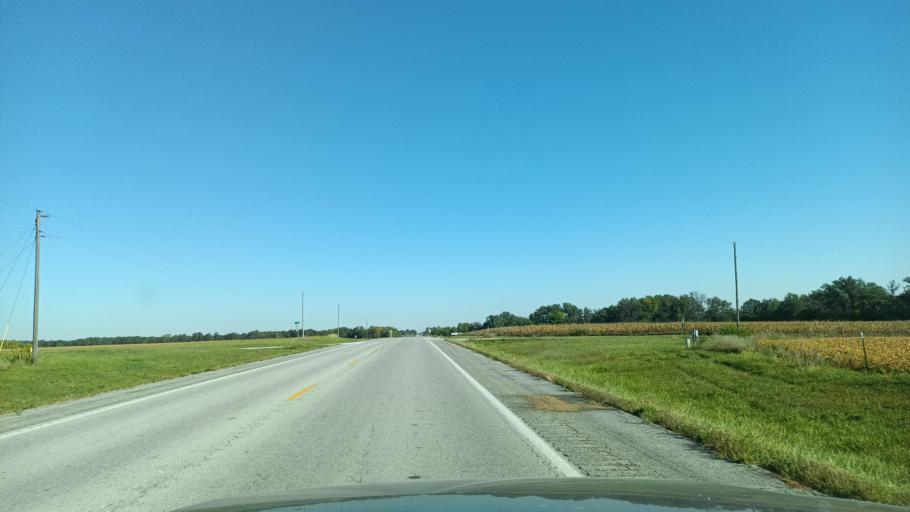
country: US
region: Missouri
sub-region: Audrain County
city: Vandalia
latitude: 39.2948
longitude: -91.6439
